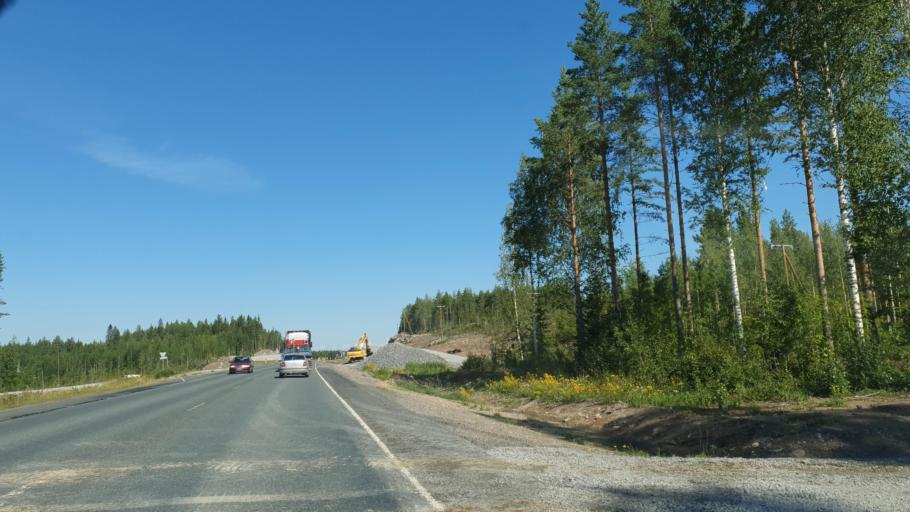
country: FI
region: Northern Savo
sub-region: Ylae-Savo
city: Lapinlahti
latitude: 63.2785
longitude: 27.4573
